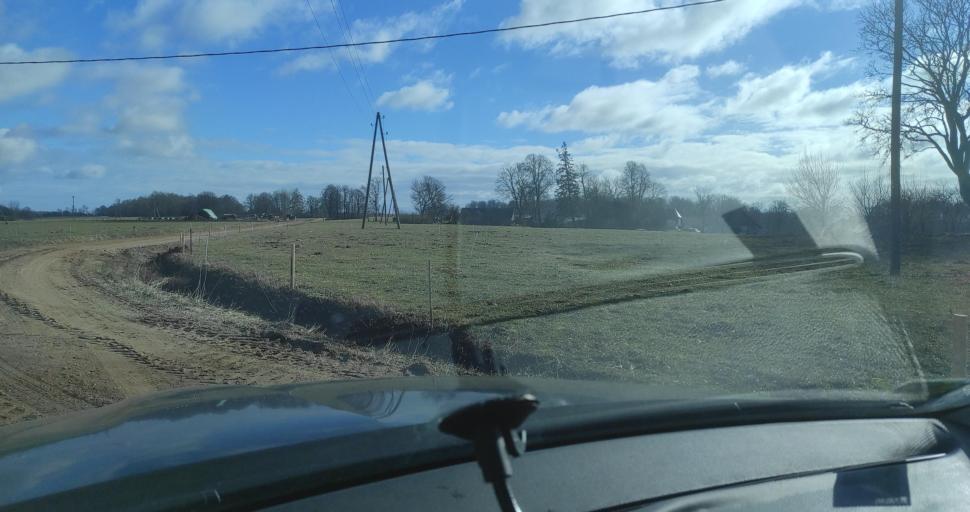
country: LV
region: Vainode
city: Vainode
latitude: 56.5150
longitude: 21.8576
